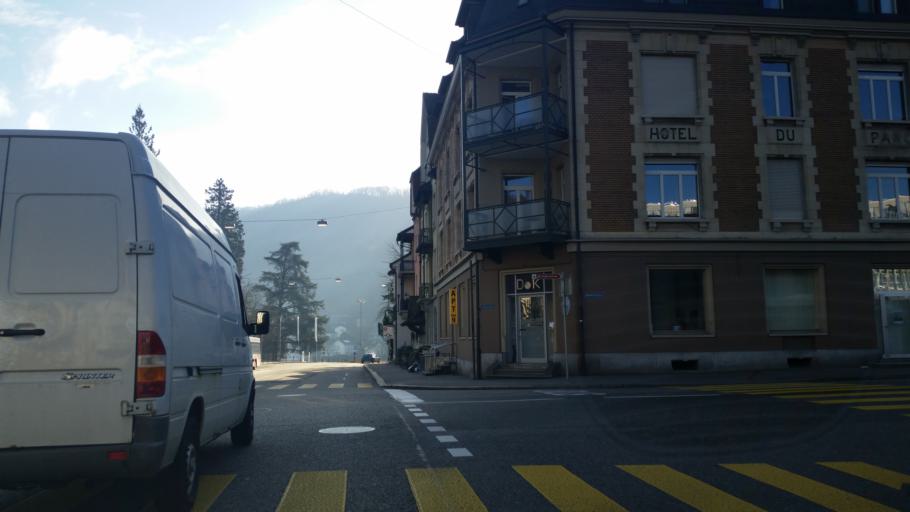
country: CH
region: Aargau
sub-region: Bezirk Baden
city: Baden
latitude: 47.4784
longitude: 8.3086
